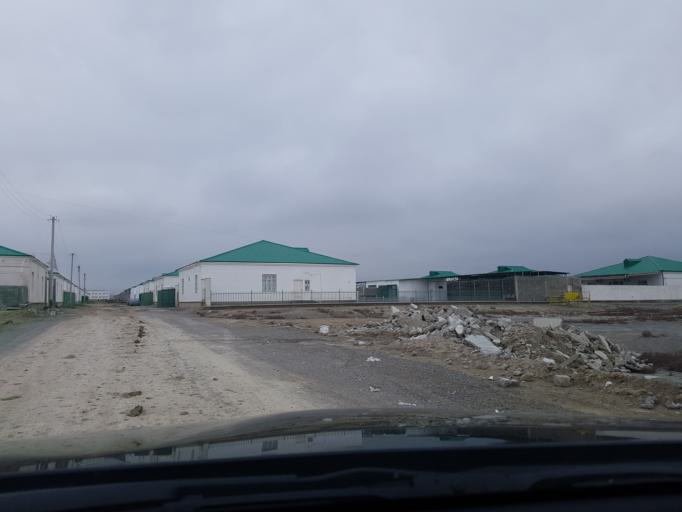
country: TM
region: Ahal
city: Abadan
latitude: 38.1576
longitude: 57.9500
